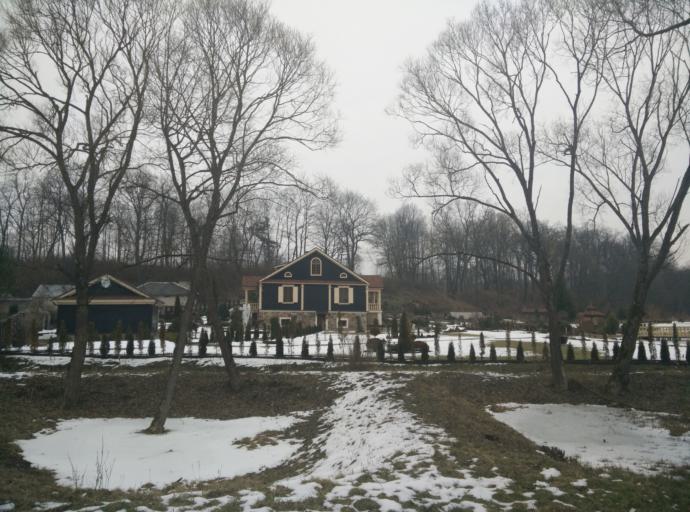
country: LT
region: Vilnius County
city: Rasos
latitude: 54.6885
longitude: 25.3584
